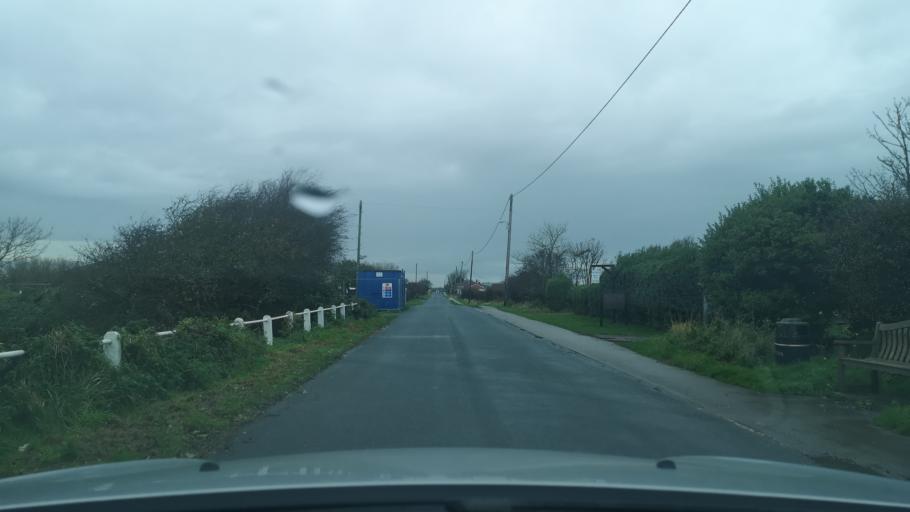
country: GB
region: England
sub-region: East Riding of Yorkshire
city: Easington
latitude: 53.6218
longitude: 0.1284
